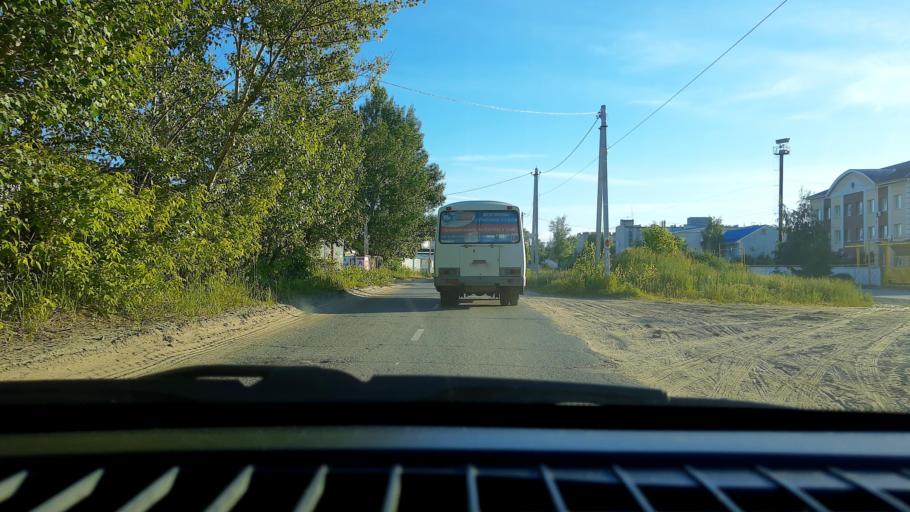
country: RU
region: Nizjnij Novgorod
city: Dzerzhinsk
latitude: 56.2456
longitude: 43.4947
